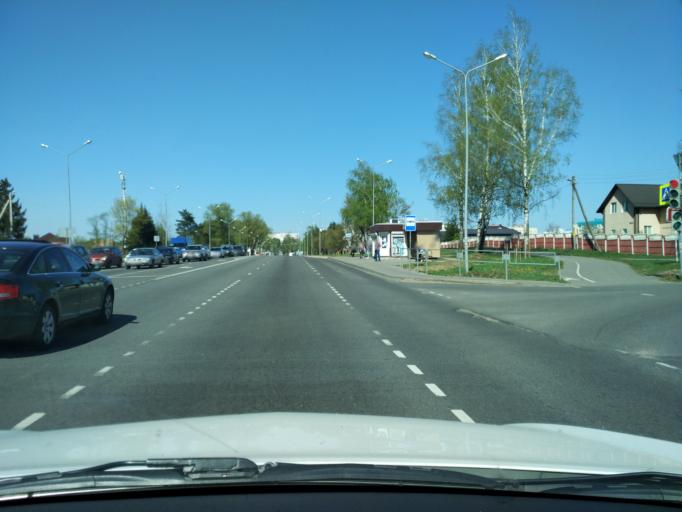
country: BY
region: Minsk
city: Borovlyany
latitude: 53.9959
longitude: 27.6735
